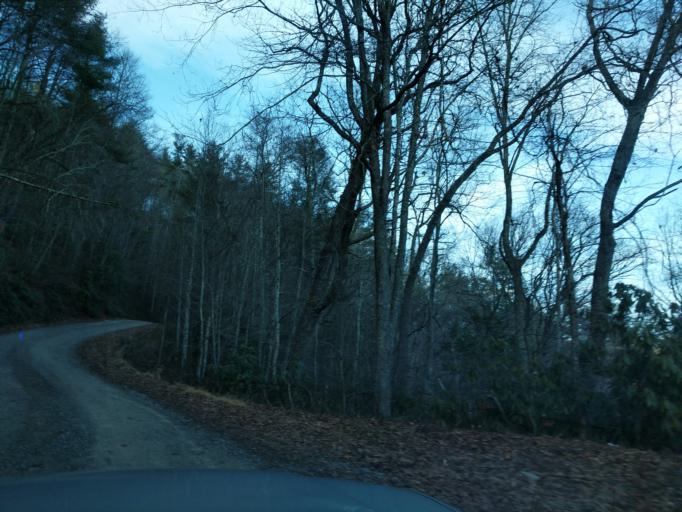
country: US
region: North Carolina
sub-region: Haywood County
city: Cove Creek
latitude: 35.7439
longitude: -83.0424
